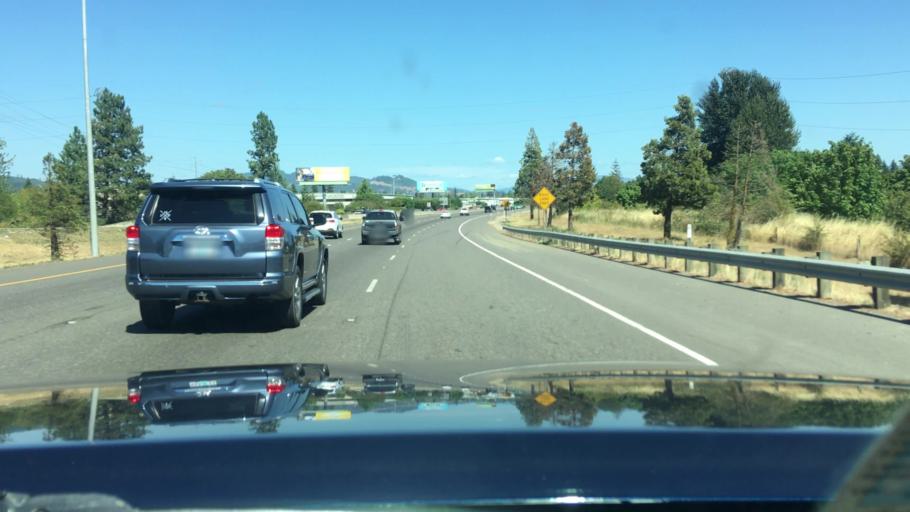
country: US
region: Oregon
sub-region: Lane County
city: Springfield
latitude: 44.0628
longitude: -123.0438
